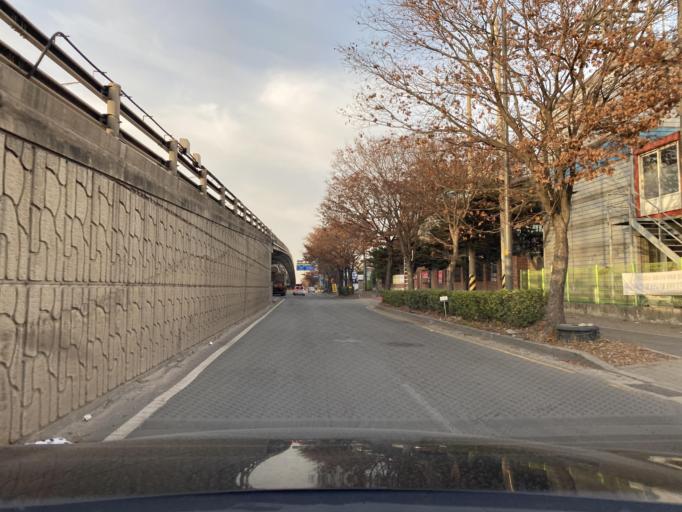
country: KR
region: Incheon
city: Incheon
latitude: 37.5051
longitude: 126.6486
